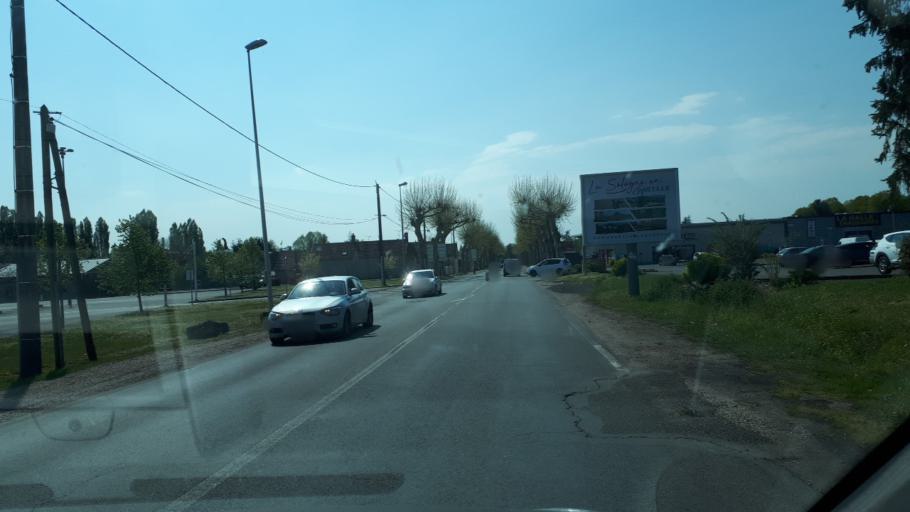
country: FR
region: Centre
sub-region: Departement du Loir-et-Cher
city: Romorantin-Lanthenay
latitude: 47.3766
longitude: 1.7364
